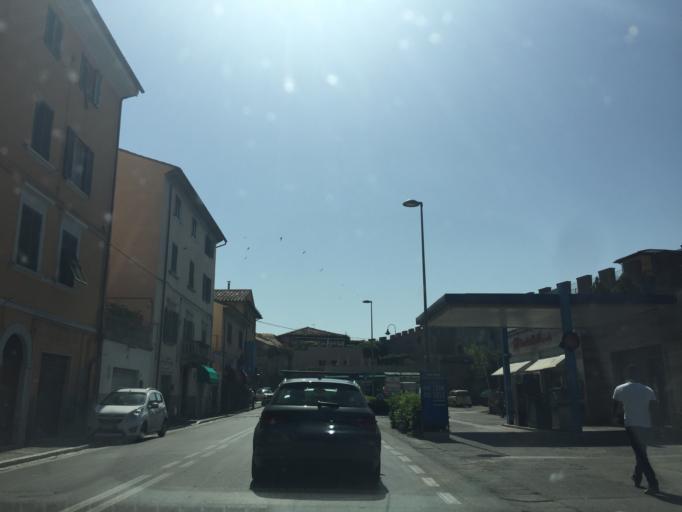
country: IT
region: Tuscany
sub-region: Province of Pisa
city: Pisa
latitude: 43.7230
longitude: 10.4008
